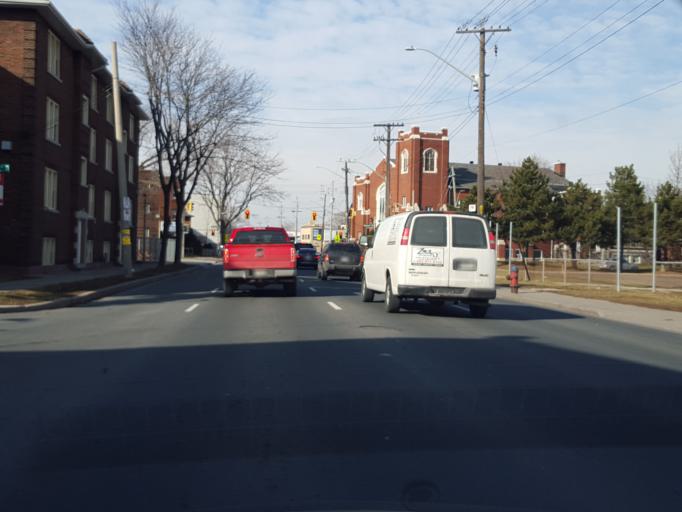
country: CA
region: Ontario
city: Hamilton
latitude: 43.2496
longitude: -79.8315
